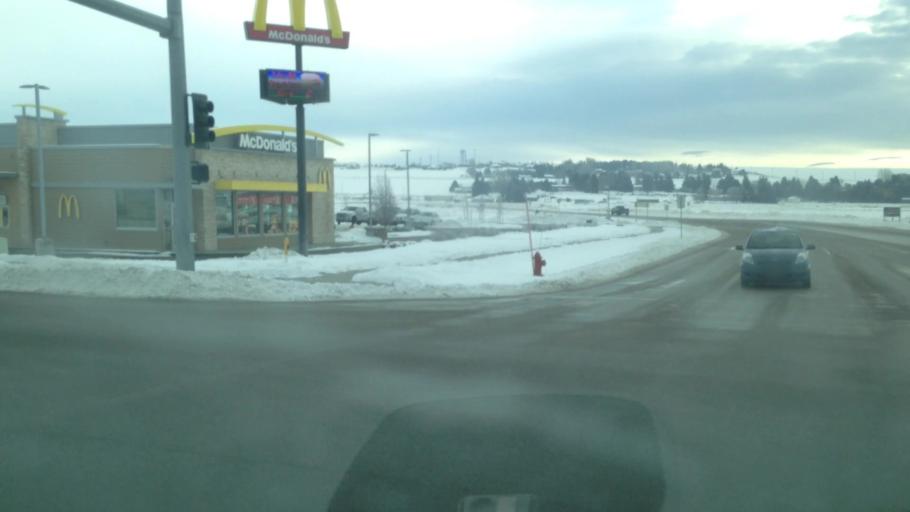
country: US
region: Idaho
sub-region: Madison County
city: Rexburg
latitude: 43.8039
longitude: -111.8088
